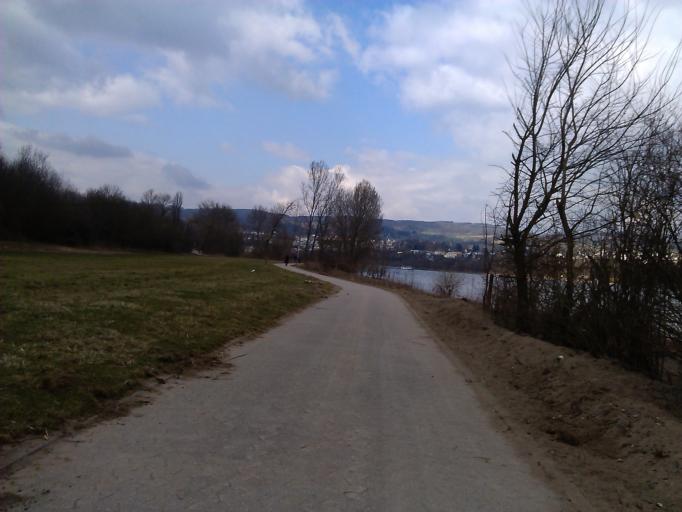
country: DE
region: Rheinland-Pfalz
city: Weissenthurm
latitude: 50.4374
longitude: 7.4415
